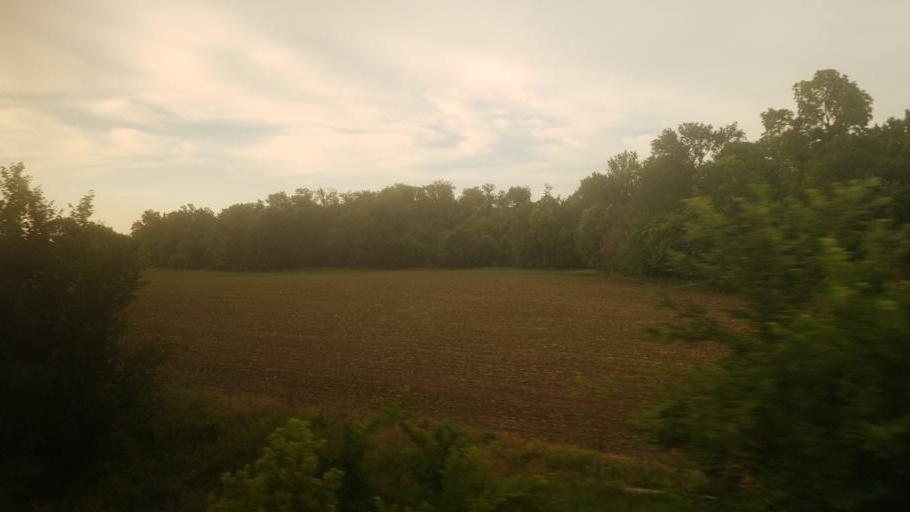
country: US
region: Kansas
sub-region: Osage County
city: Osage City
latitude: 38.5179
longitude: -95.9745
